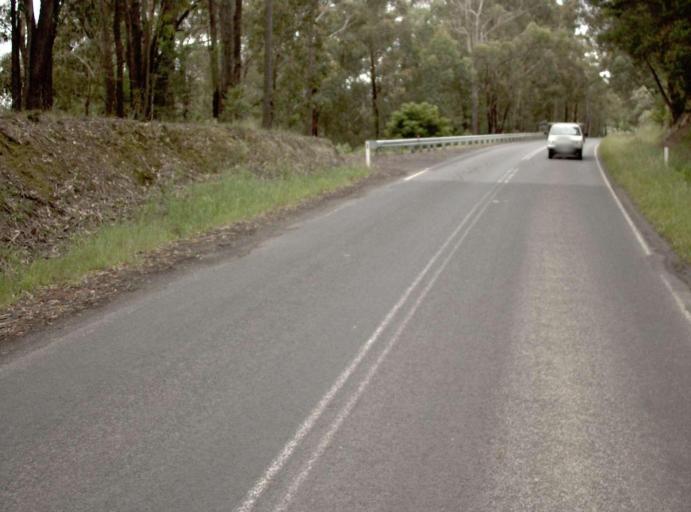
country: AU
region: Victoria
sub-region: Baw Baw
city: Warragul
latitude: -38.0473
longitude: 145.9592
